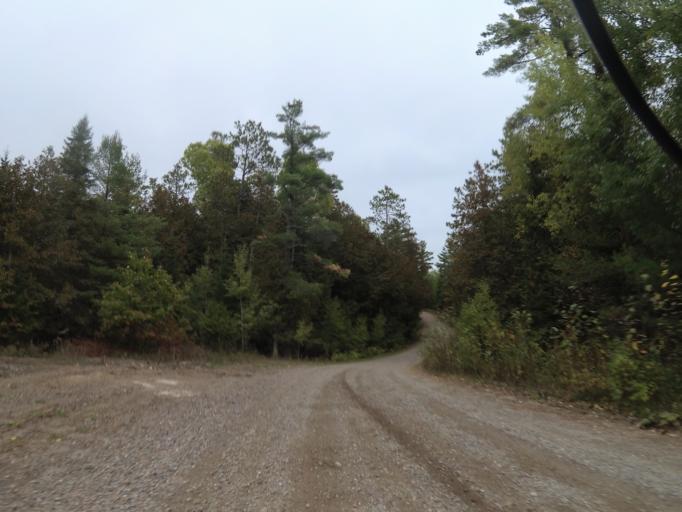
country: CA
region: Ontario
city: Renfrew
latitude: 45.2047
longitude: -77.0933
